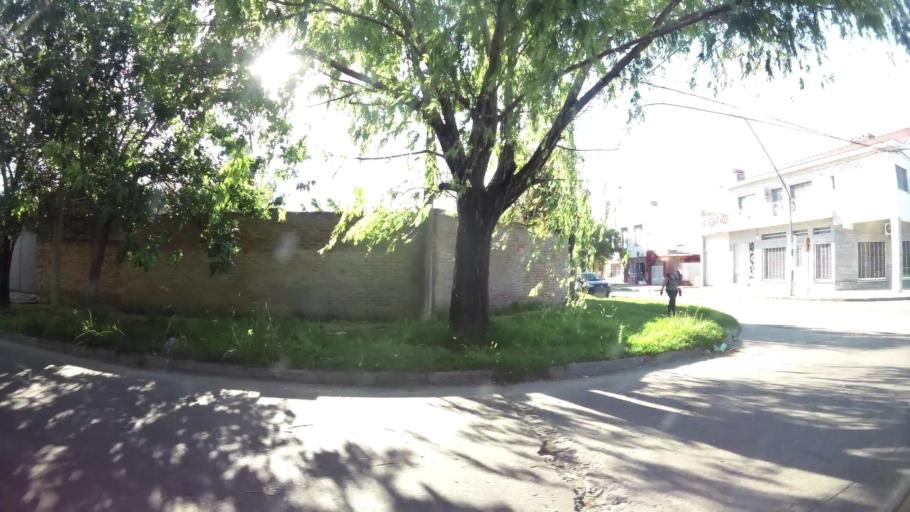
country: AR
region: Santa Fe
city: Santa Fe de la Vera Cruz
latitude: -31.6108
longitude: -60.7017
